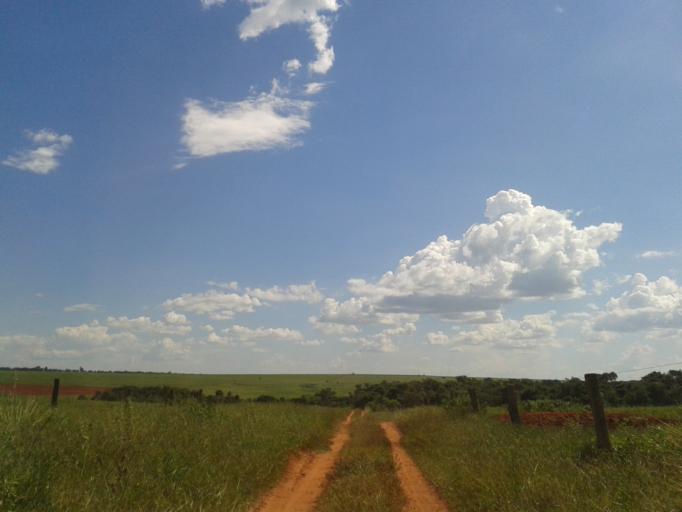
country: BR
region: Minas Gerais
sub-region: Santa Vitoria
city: Santa Vitoria
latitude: -19.1160
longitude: -50.5003
